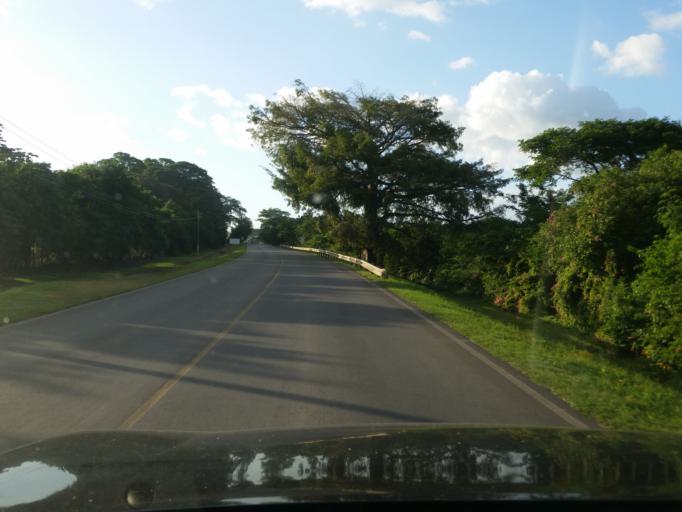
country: NI
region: Granada
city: Nandaime
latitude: 11.7477
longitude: -86.0283
